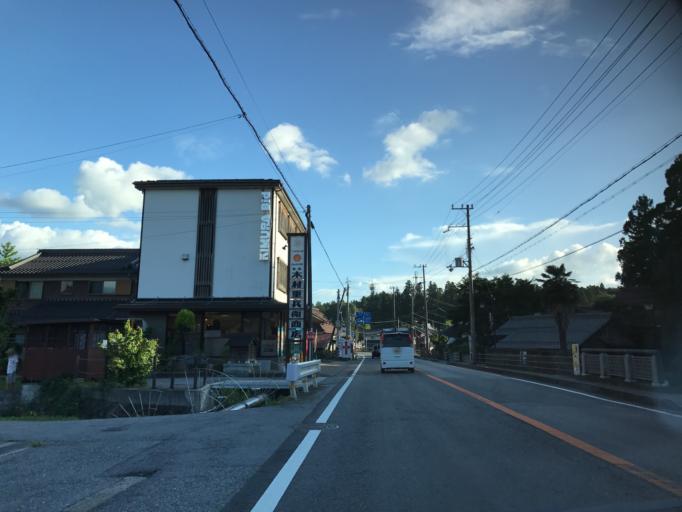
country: JP
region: Shiga Prefecture
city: Hikone
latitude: 35.2256
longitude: 136.2930
